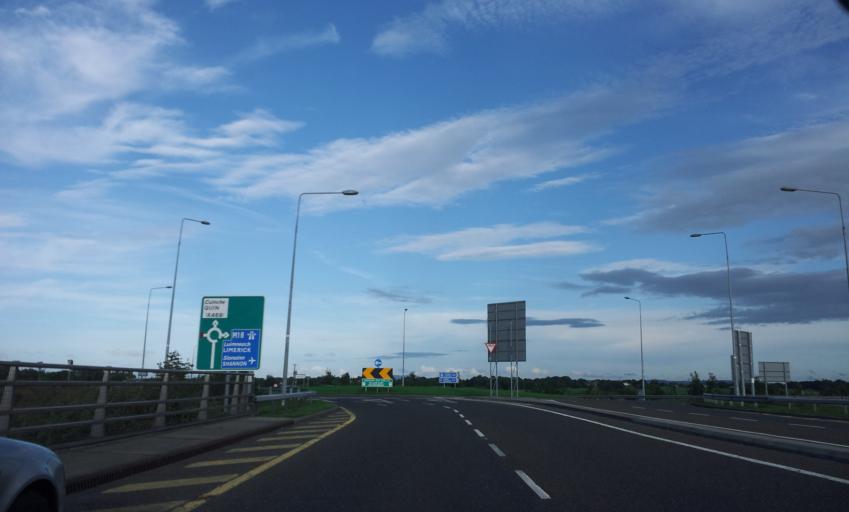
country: IE
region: Munster
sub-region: An Clar
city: Ennis
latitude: 52.8275
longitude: -8.9385
